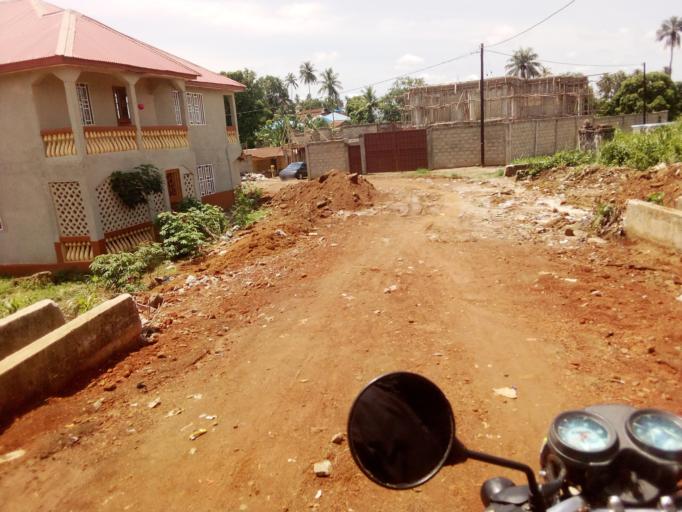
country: SL
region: Western Area
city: Waterloo
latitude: 8.3365
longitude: -13.0687
